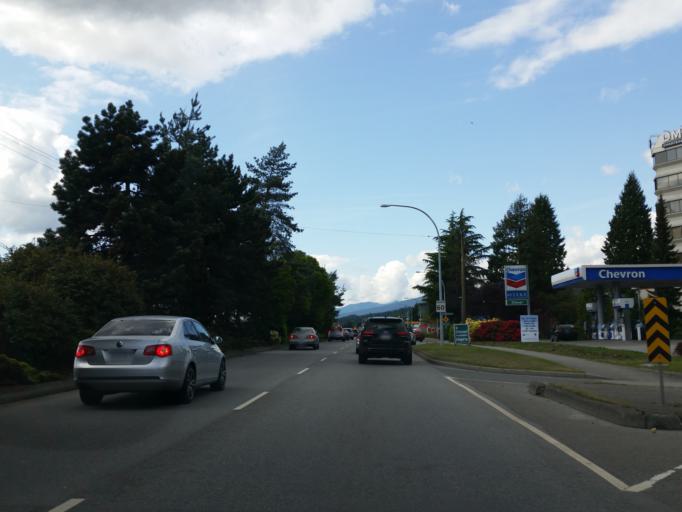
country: CA
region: British Columbia
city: Coquitlam
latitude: 49.2723
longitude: -122.7876
